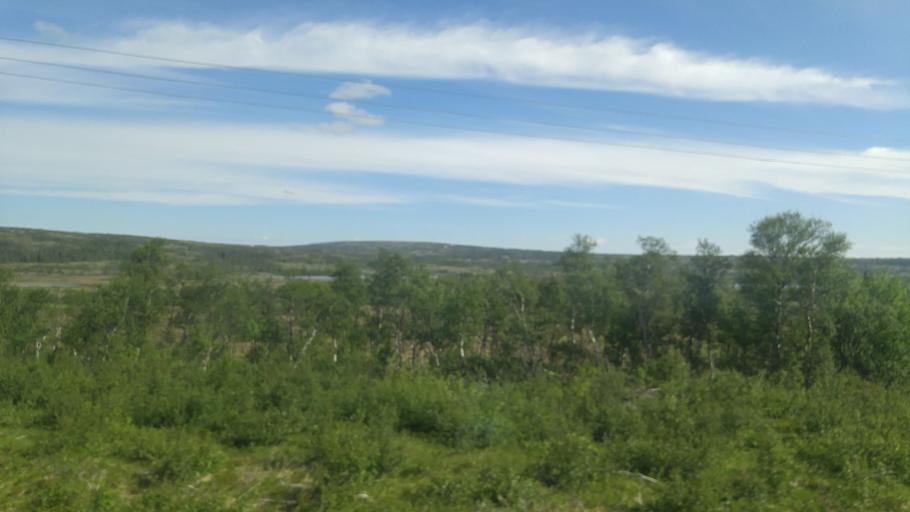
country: NO
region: Nord-Trondelag
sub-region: Meraker
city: Meraker
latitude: 63.3186
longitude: 12.1906
